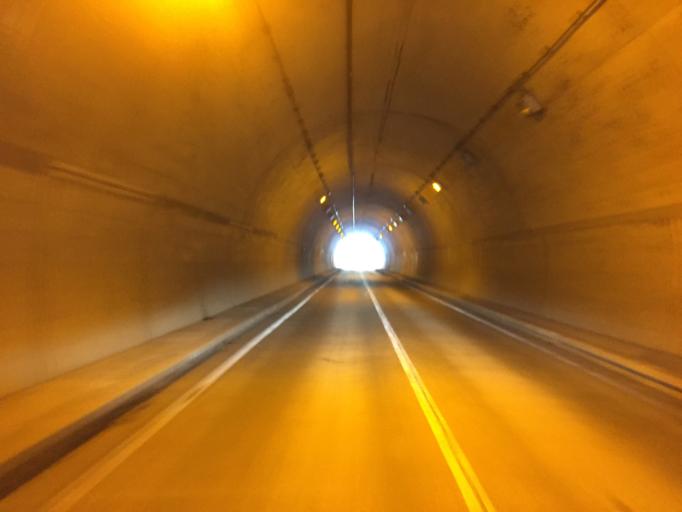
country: JP
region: Fukushima
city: Inawashiro
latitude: 37.4615
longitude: 139.9674
